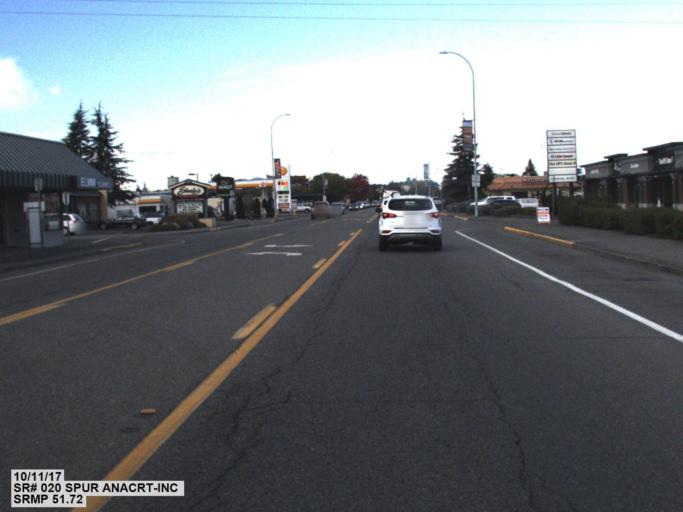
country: US
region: Washington
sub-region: Jefferson County
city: Port Hadlock-Irondale
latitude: 48.0156
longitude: -122.8311
